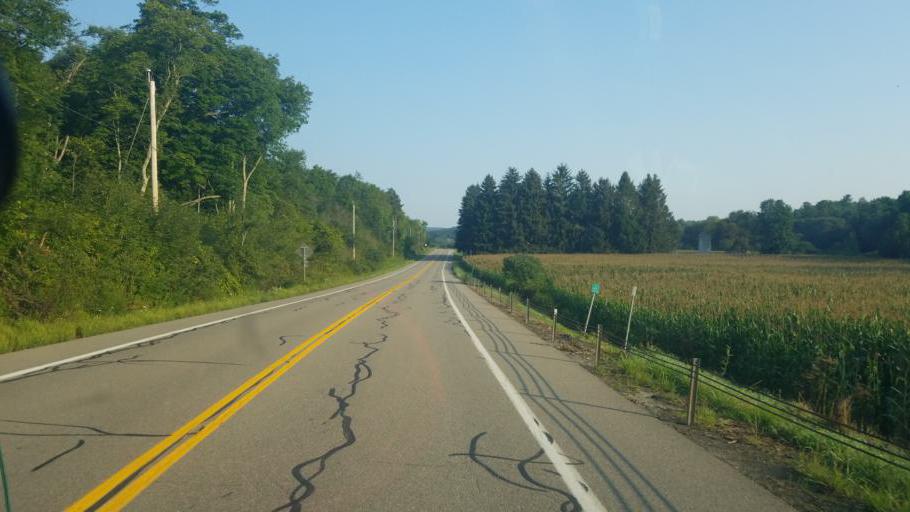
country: US
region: Pennsylvania
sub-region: Tioga County
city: Westfield
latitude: 42.0097
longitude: -77.5173
